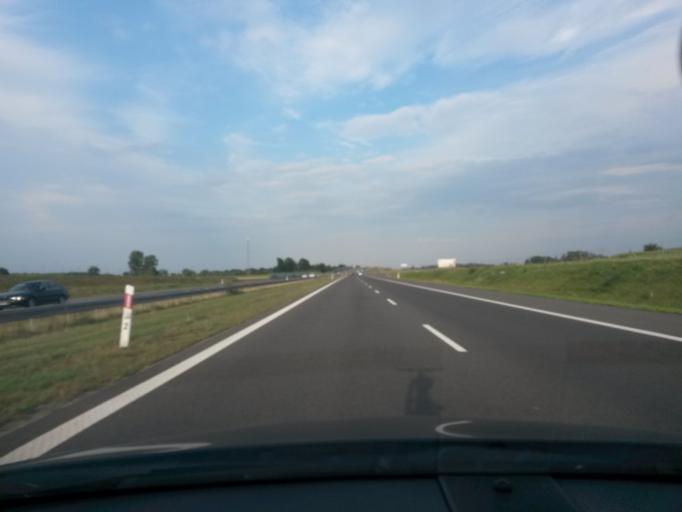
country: PL
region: Lodz Voivodeship
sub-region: Powiat zgierski
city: Zgierz
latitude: 51.8980
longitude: 19.5008
